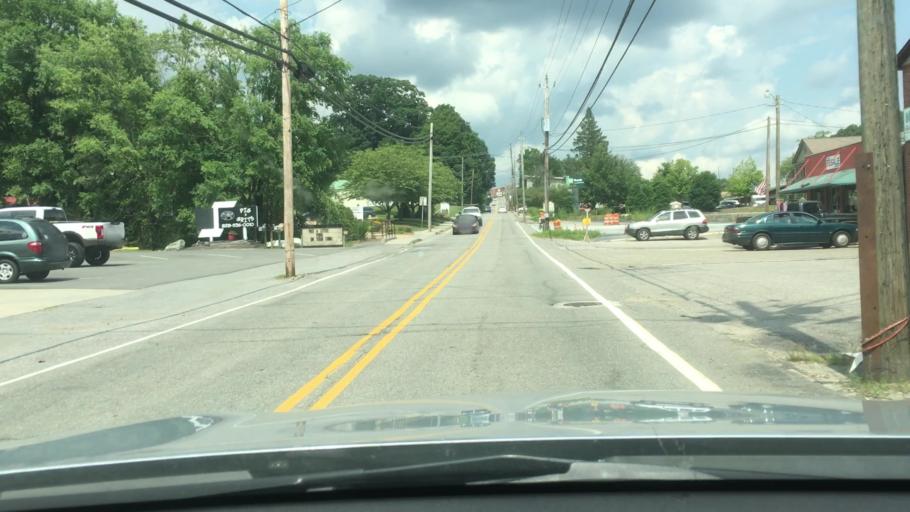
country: US
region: North Carolina
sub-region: Yancey County
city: Burnsville
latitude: 35.9148
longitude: -82.3085
